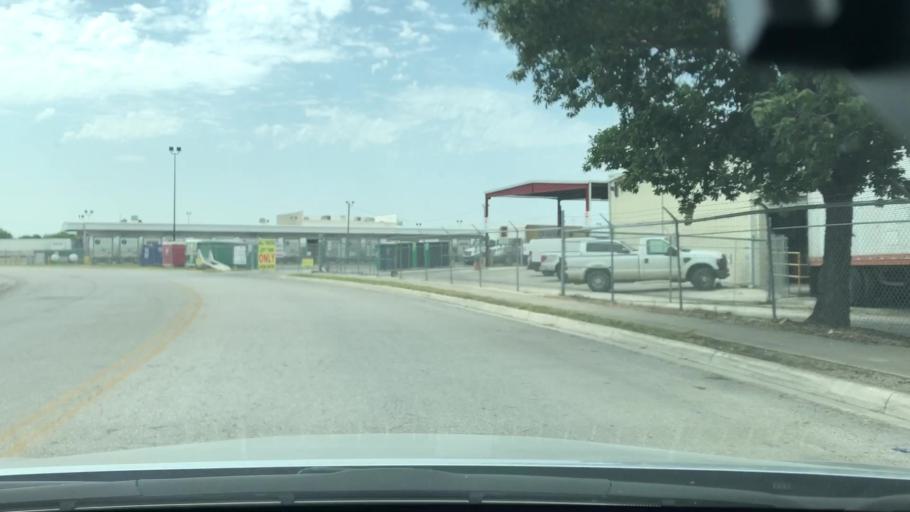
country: US
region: Texas
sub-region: Bexar County
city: Kirby
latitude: 29.4597
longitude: -98.4018
